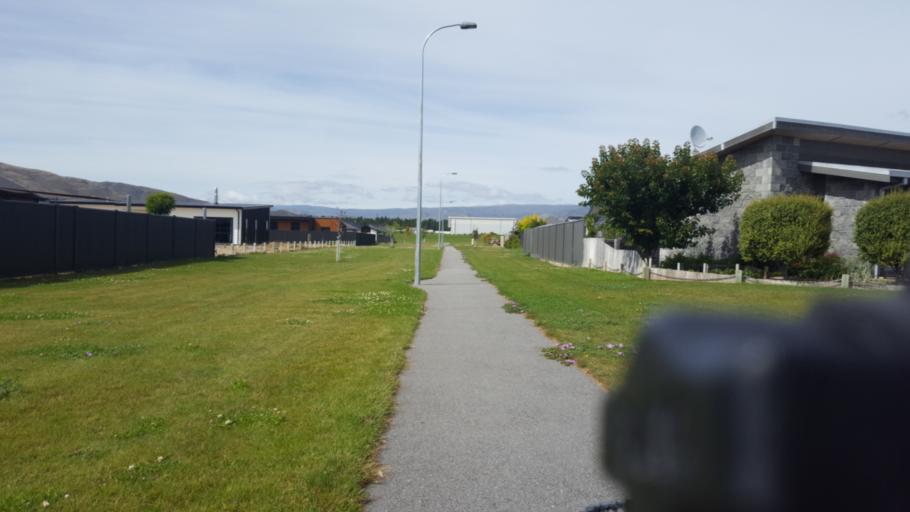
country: NZ
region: Otago
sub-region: Queenstown-Lakes District
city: Wanaka
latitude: -45.0468
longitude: 169.1884
